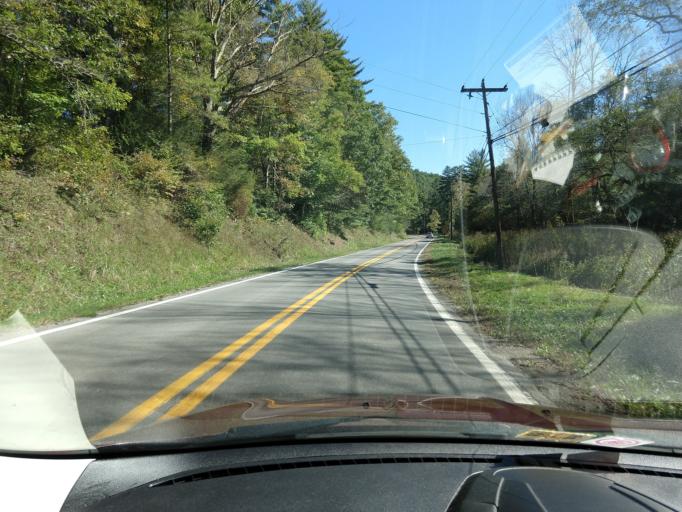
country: US
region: West Virginia
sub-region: Pocahontas County
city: Marlinton
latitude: 38.2145
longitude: -80.0435
